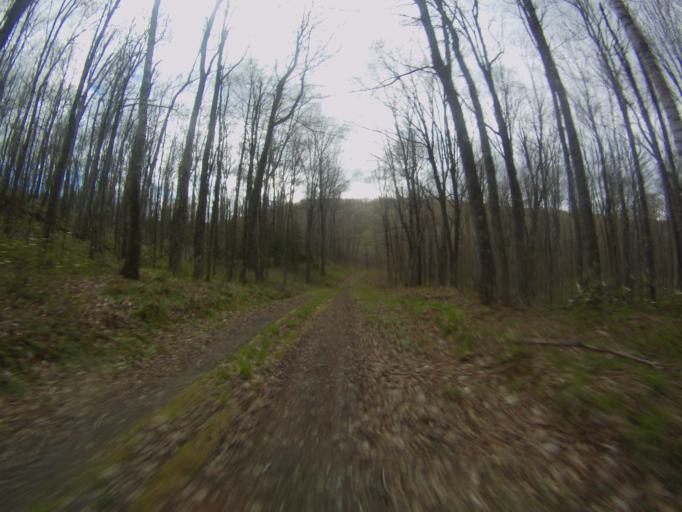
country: US
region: Vermont
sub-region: Addison County
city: Bristol
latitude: 44.0480
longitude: -73.0563
